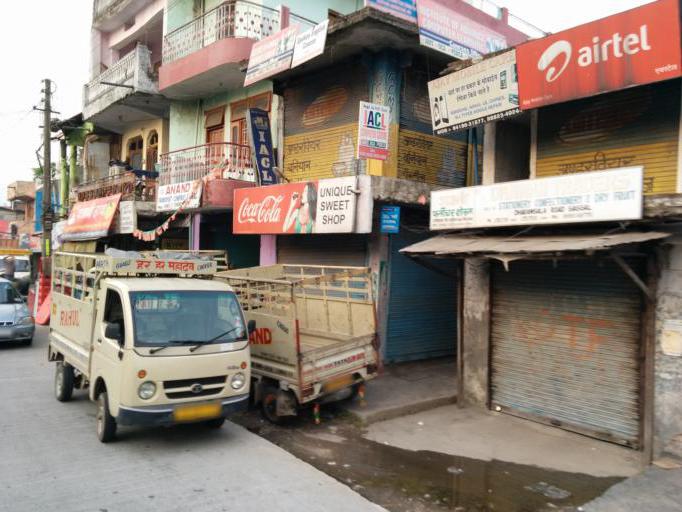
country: IN
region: Himachal Pradesh
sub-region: Kangra
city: Kangra
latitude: 32.1540
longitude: 76.2702
